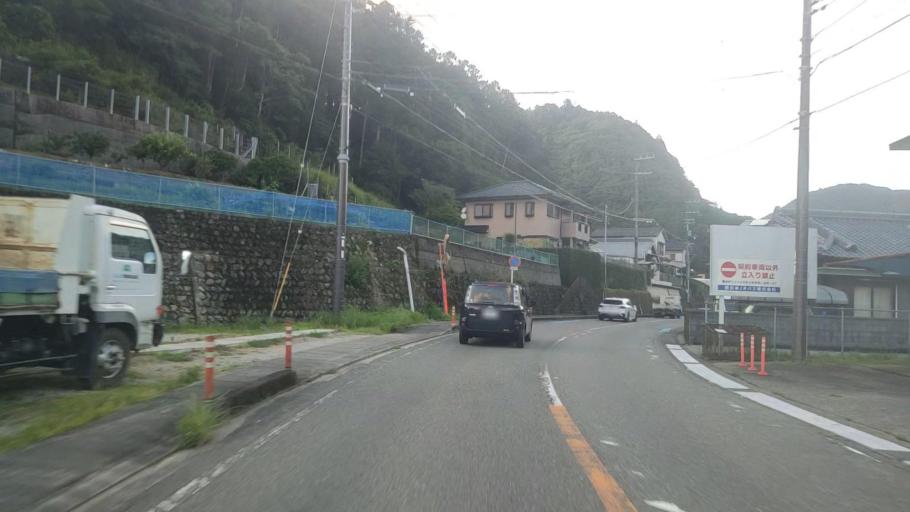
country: JP
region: Wakayama
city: Tanabe
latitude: 33.7947
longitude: 135.5185
